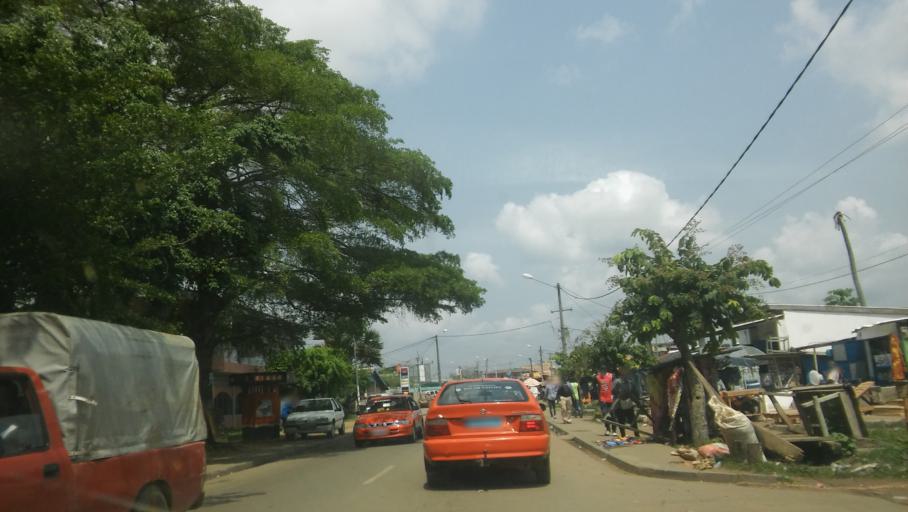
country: CI
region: Sud-Comoe
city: Grand-Bassam
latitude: 5.2042
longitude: -3.7357
